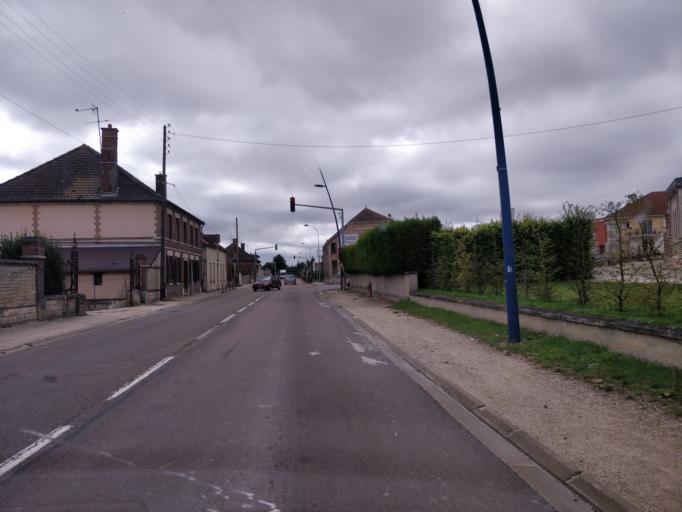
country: FR
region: Champagne-Ardenne
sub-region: Departement de l'Aube
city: Saint-Germain
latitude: 48.2584
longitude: 4.0311
